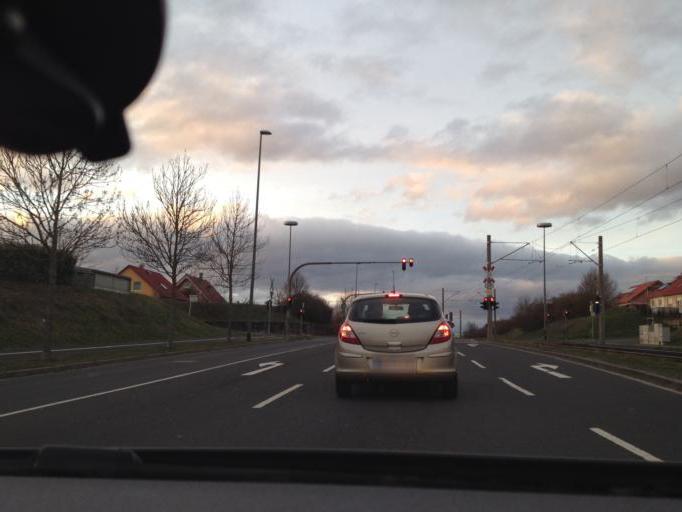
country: DE
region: Bavaria
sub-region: Regierungsbezirk Unterfranken
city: Eibelstadt
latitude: 49.7244
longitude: 9.9673
